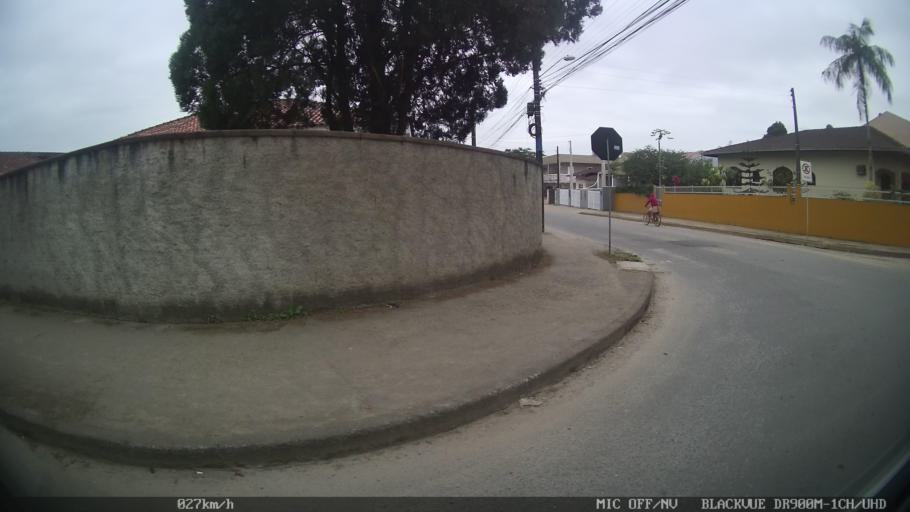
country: BR
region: Santa Catarina
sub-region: Joinville
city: Joinville
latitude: -26.3526
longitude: -48.8277
